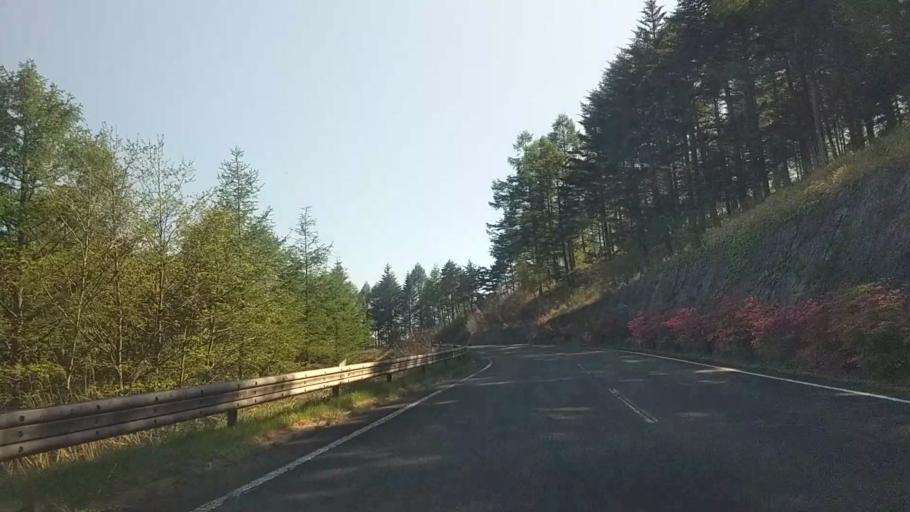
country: JP
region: Yamanashi
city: Nirasaki
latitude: 35.9228
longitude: 138.3981
